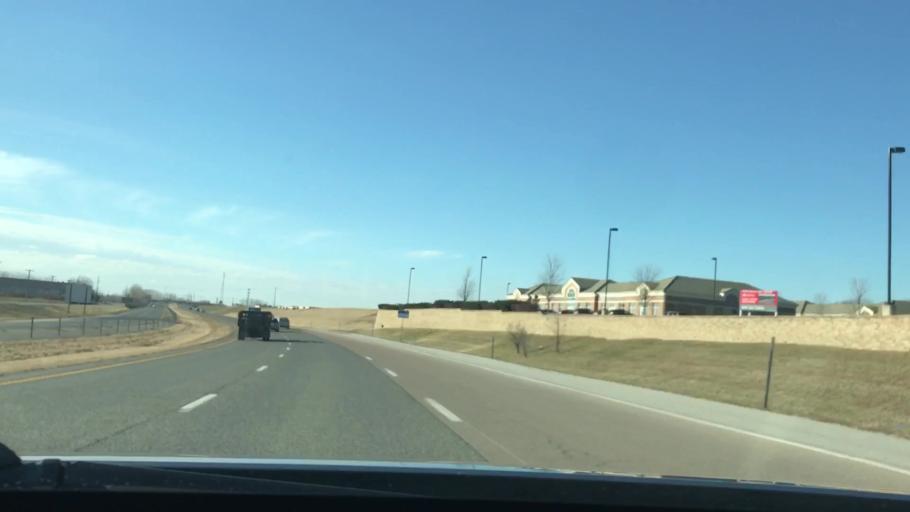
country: US
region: Missouri
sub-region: Platte County
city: Riverside
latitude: 39.1663
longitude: -94.6023
